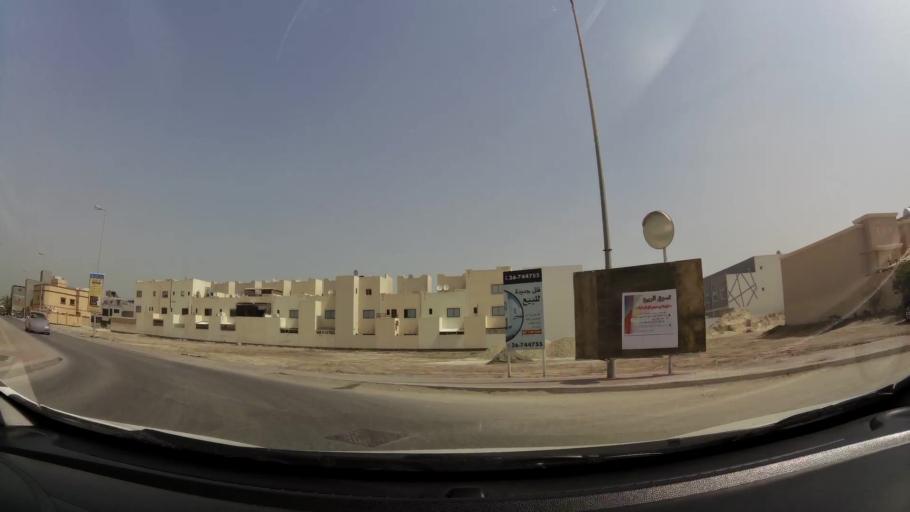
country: BH
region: Manama
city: Jidd Hafs
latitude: 26.2250
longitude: 50.4808
